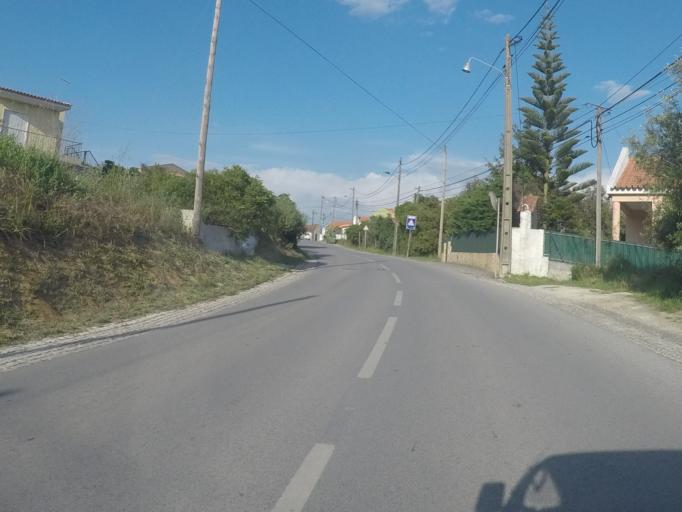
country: PT
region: Setubal
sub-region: Sesimbra
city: Sesimbra
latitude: 38.4768
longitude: -9.1629
